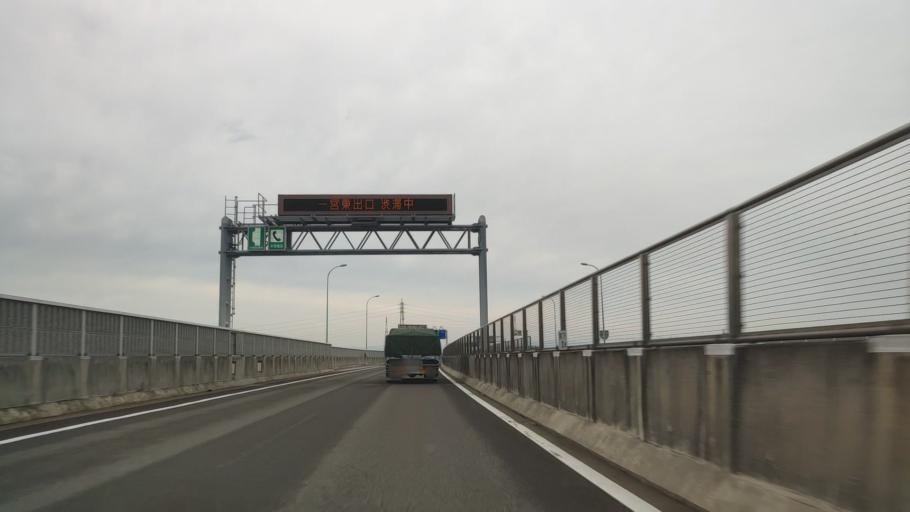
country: JP
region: Aichi
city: Iwakura
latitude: 35.2431
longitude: 136.8460
